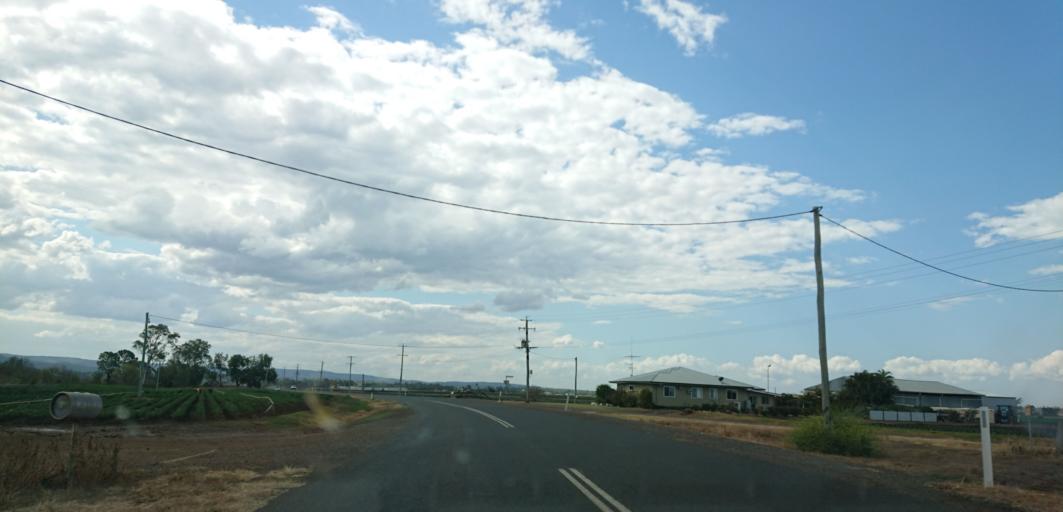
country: AU
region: Queensland
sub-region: Lockyer Valley
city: Gatton
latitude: -27.5930
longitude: 152.2264
